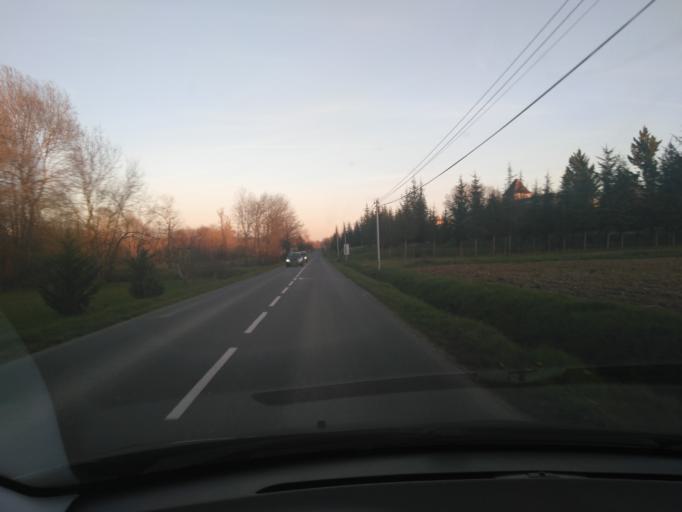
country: FR
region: Aquitaine
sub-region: Departement du Lot-et-Garonne
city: Saint-Hilaire
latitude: 44.5387
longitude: 0.6913
